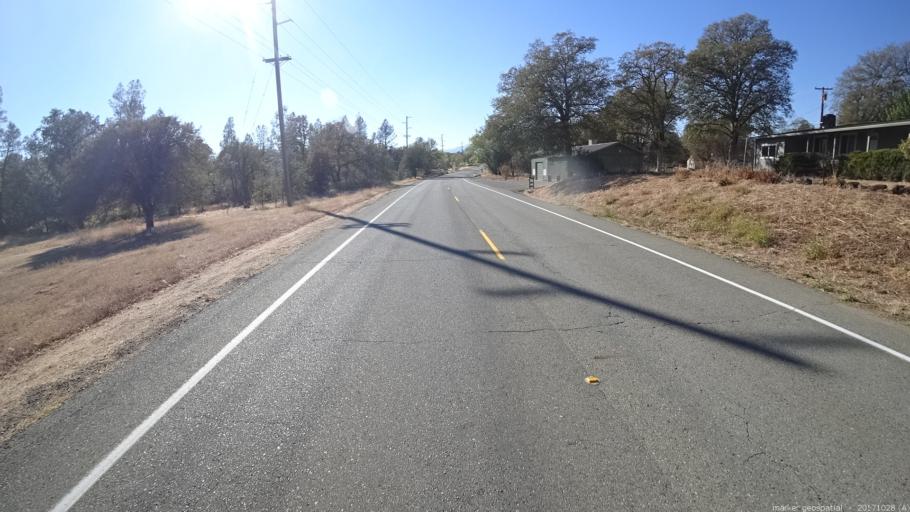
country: US
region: California
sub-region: Shasta County
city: Central Valley (historical)
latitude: 40.6363
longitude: -122.3822
